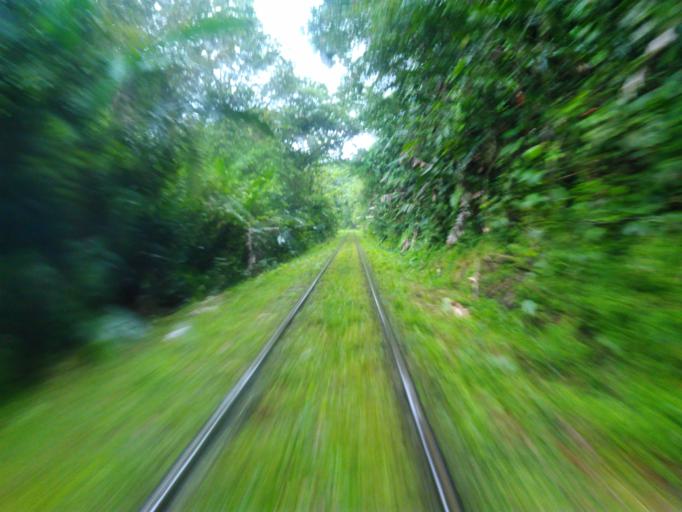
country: CO
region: Valle del Cauca
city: Buenaventura
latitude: 3.8441
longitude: -76.8809
